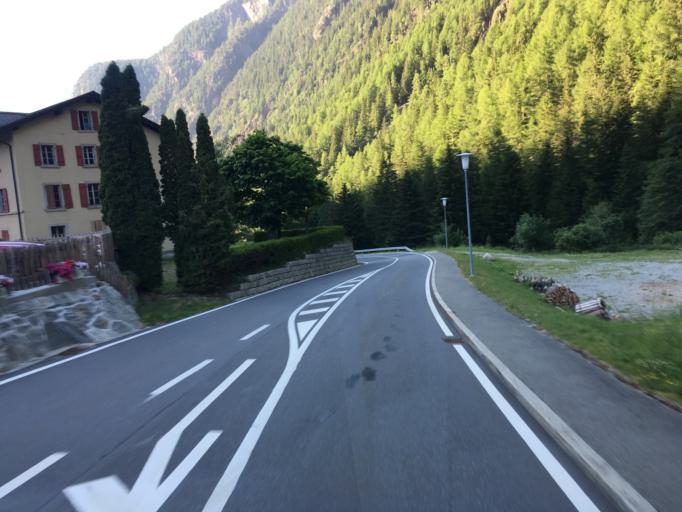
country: CH
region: Valais
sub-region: Martigny District
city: Martigny-Combe
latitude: 46.0558
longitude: 6.9962
